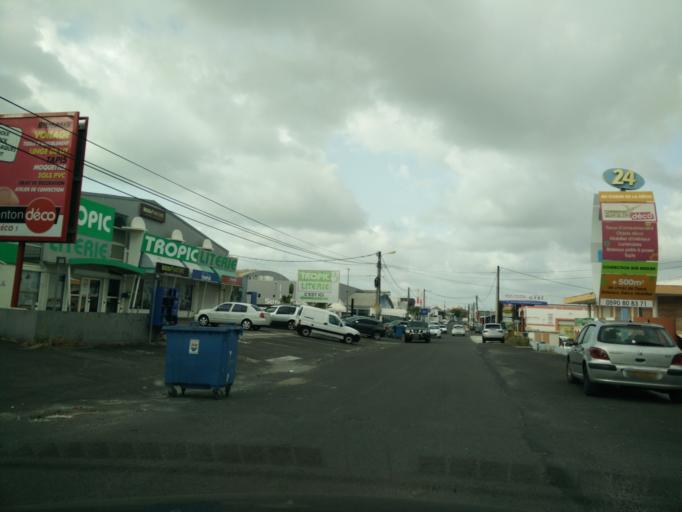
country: GP
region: Guadeloupe
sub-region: Guadeloupe
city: Pointe-a-Pitre
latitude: 16.2404
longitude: -61.5646
